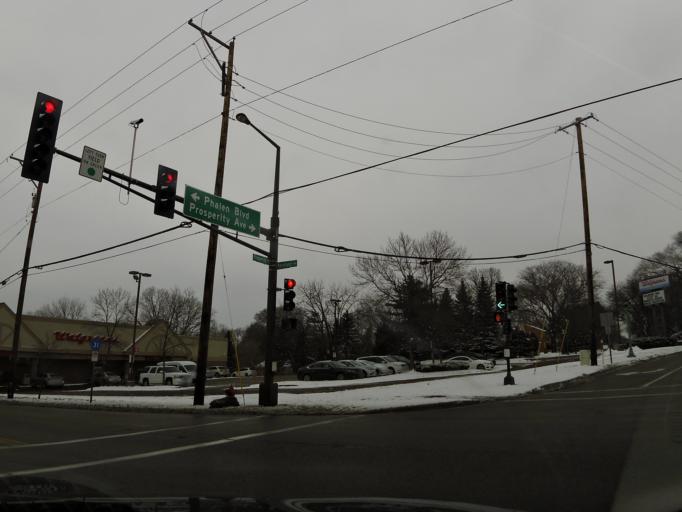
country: US
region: Minnesota
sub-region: Ramsey County
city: Maplewood
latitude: 44.9775
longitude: -93.0406
